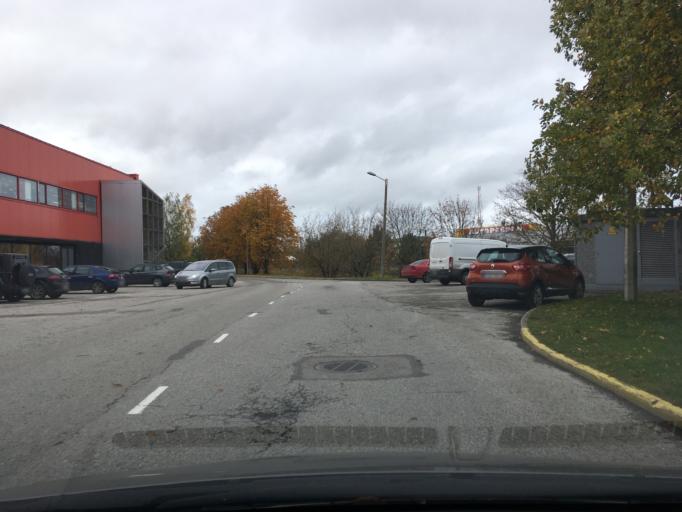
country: EE
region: Harju
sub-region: Tallinna linn
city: Tallinn
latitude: 59.3942
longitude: 24.7213
